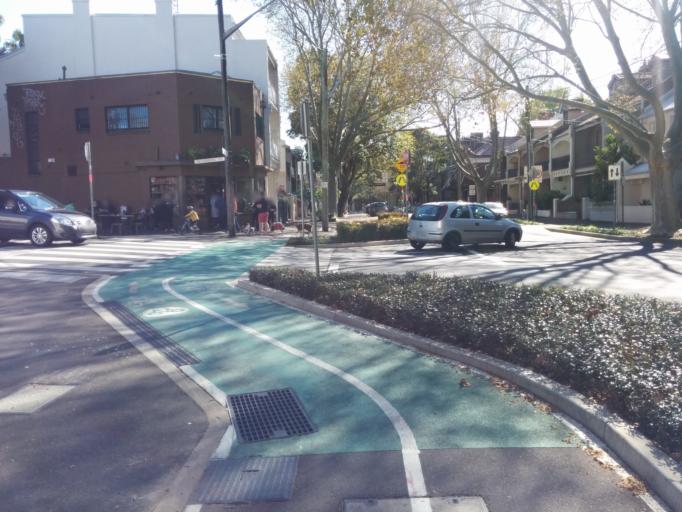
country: AU
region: New South Wales
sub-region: City of Sydney
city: Darlinghurst
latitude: -33.8897
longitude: 151.2150
